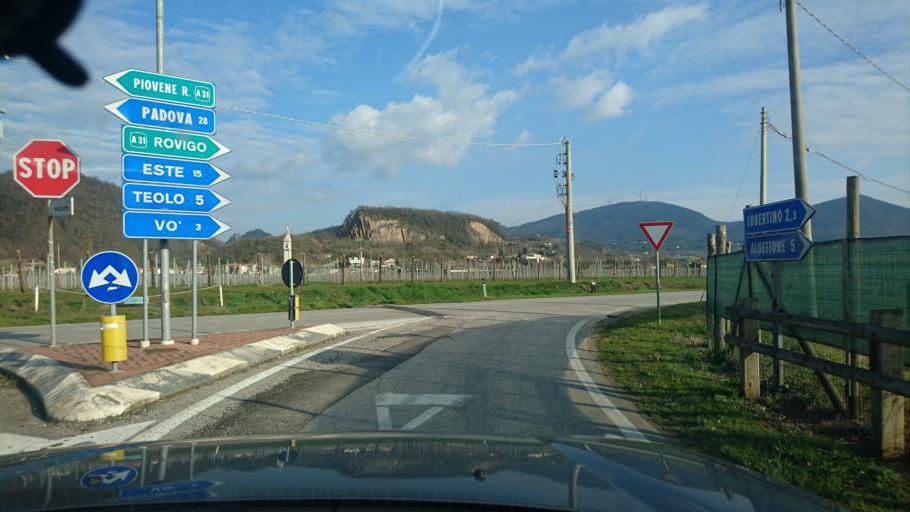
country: IT
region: Veneto
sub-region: Provincia di Padova
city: Vo
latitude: 45.3402
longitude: 11.6398
